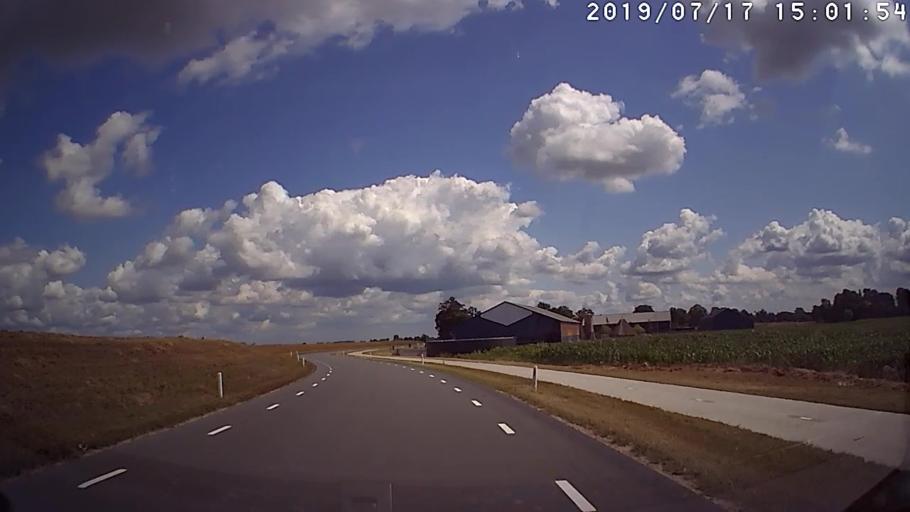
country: NL
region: Overijssel
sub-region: Gemeente Kampen
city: Kampen
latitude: 52.5244
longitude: 5.9510
